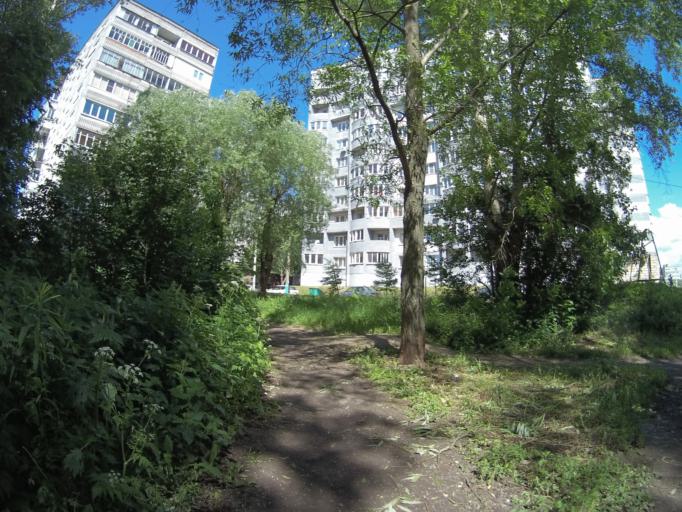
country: RU
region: Vladimir
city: Kommunar
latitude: 56.1632
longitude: 40.4495
